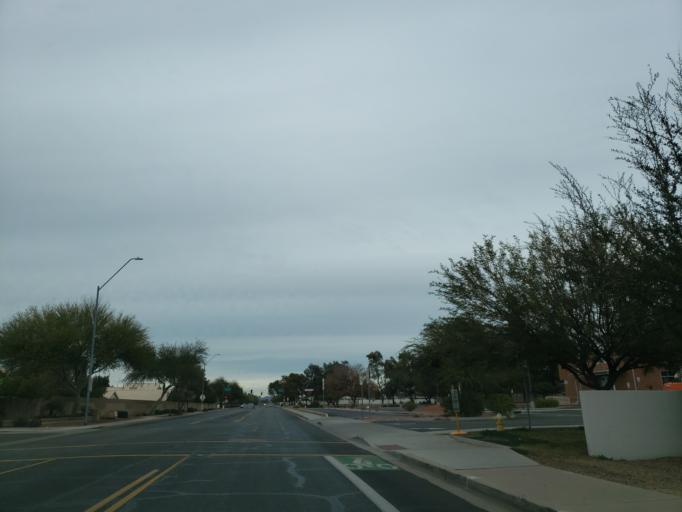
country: US
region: Arizona
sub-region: Maricopa County
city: Glendale
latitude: 33.6310
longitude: -112.0828
